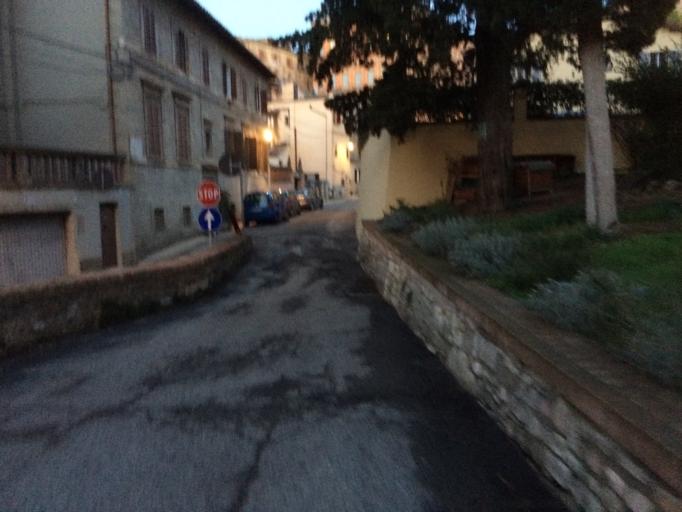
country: IT
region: Umbria
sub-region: Provincia di Perugia
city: Perugia
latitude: 43.1145
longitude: 12.3875
